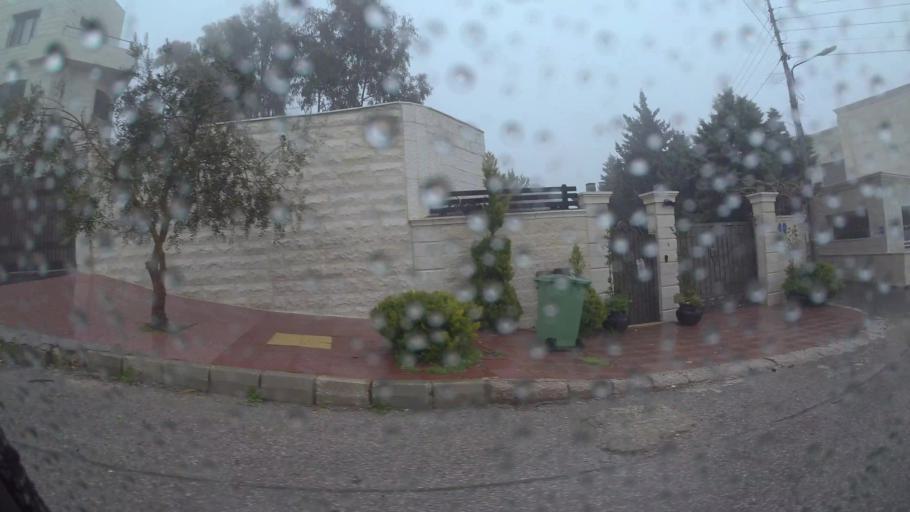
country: JO
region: Amman
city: Wadi as Sir
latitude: 31.9995
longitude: 35.8228
